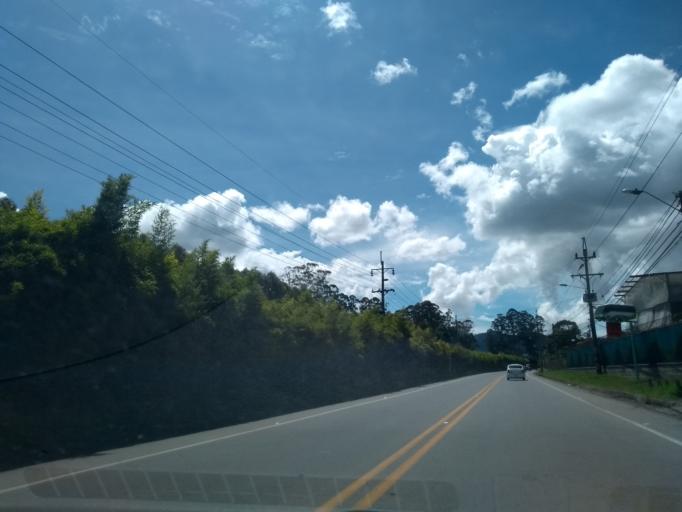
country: CO
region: Antioquia
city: La Ceja
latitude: 6.0412
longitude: -75.4090
